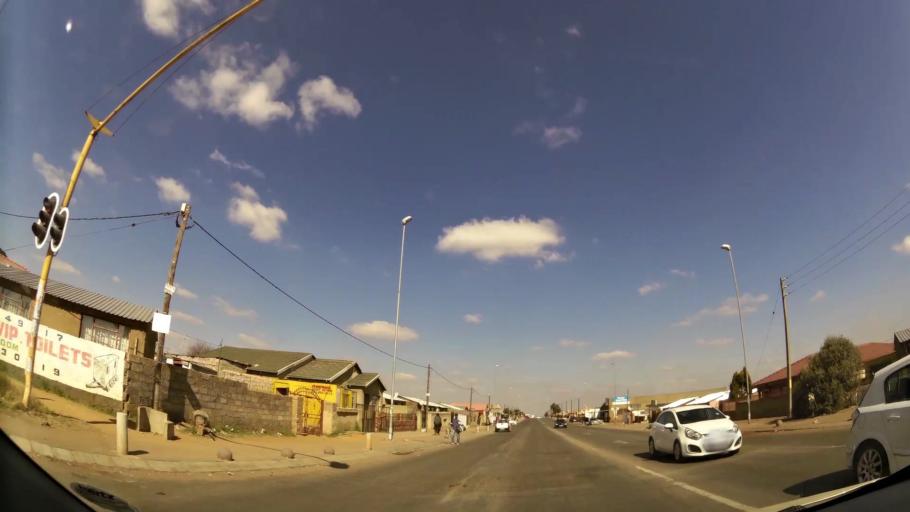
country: ZA
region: Gauteng
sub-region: West Rand District Municipality
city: Krugersdorp
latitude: -26.1541
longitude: 27.7857
